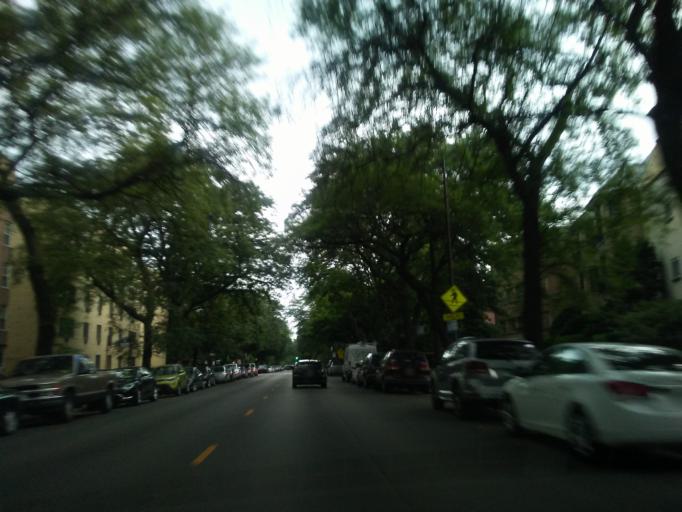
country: US
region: Illinois
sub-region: Cook County
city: Evanston
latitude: 42.0148
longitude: -87.6840
